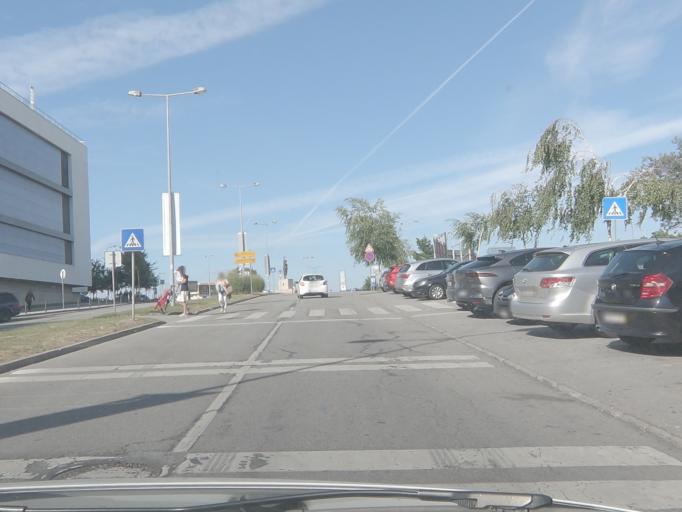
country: PT
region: Viseu
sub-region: Viseu
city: Viseu
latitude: 40.6429
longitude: -7.9110
